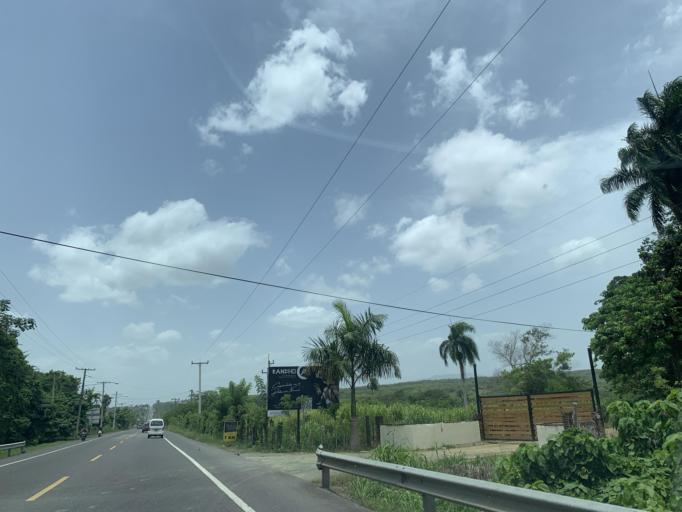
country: DO
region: Puerto Plata
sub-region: Puerto Plata
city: Puerto Plata
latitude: 19.7477
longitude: -70.6381
